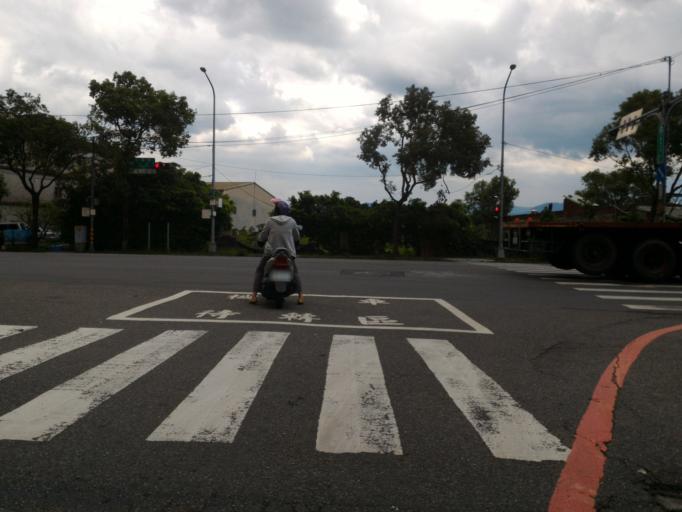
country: TW
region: Taiwan
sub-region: Taoyuan
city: Taoyuan
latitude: 24.9487
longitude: 121.3852
